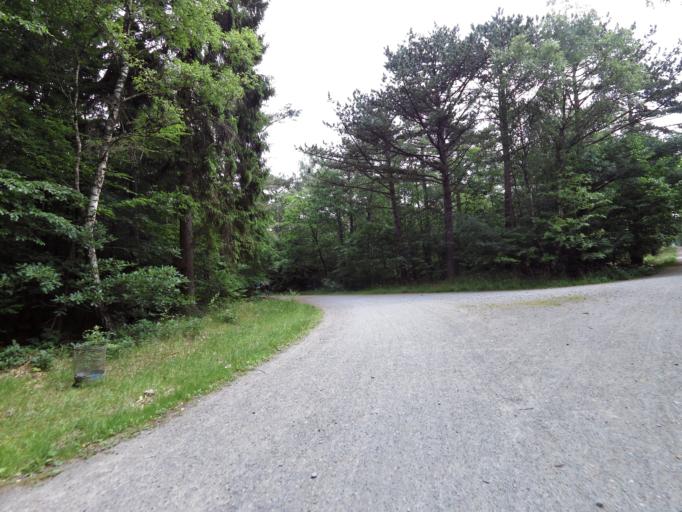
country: DE
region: Lower Saxony
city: Nordholz
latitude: 53.8546
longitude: 8.6008
